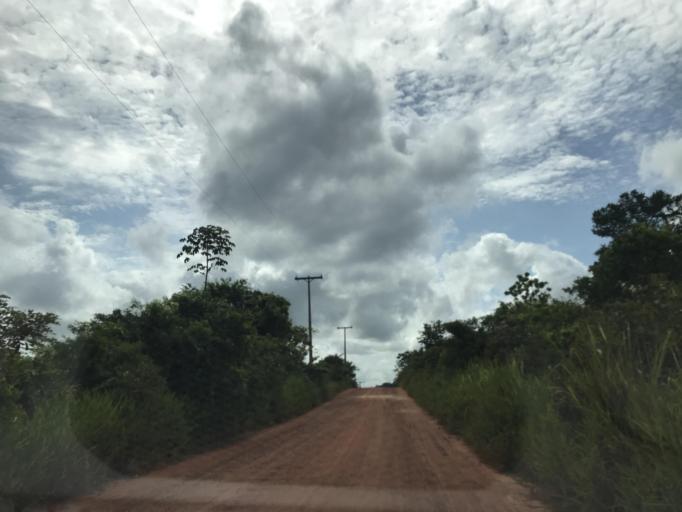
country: BR
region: Bahia
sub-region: Entre Rios
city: Entre Rios
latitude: -12.1695
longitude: -38.1518
